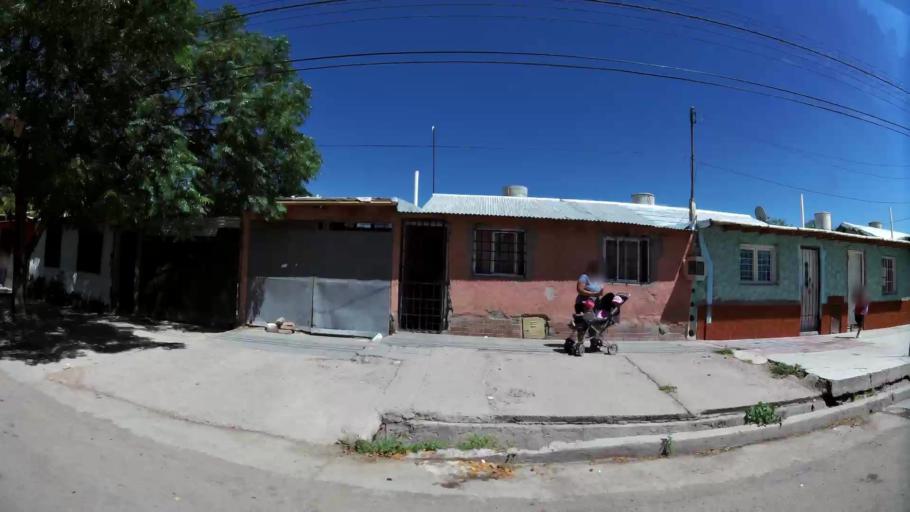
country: AR
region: Mendoza
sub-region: Departamento de Godoy Cruz
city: Godoy Cruz
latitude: -32.9318
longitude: -68.8714
